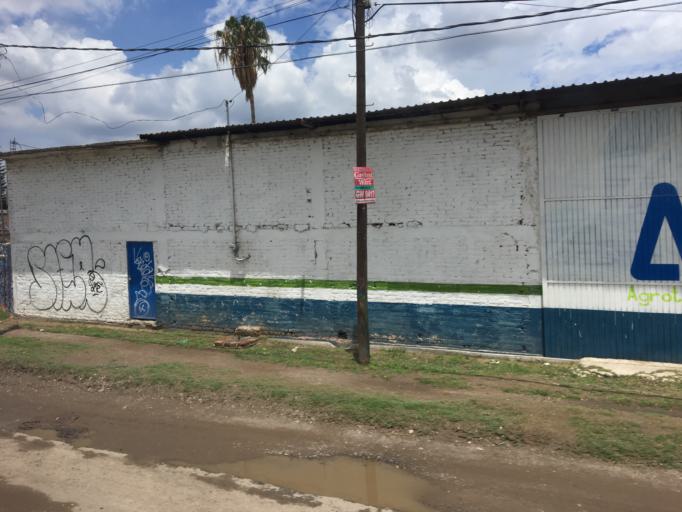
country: MX
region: Guanajuato
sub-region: Irapuato
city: Ex-Hacienda del Copal
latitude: 20.7256
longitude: -101.3448
